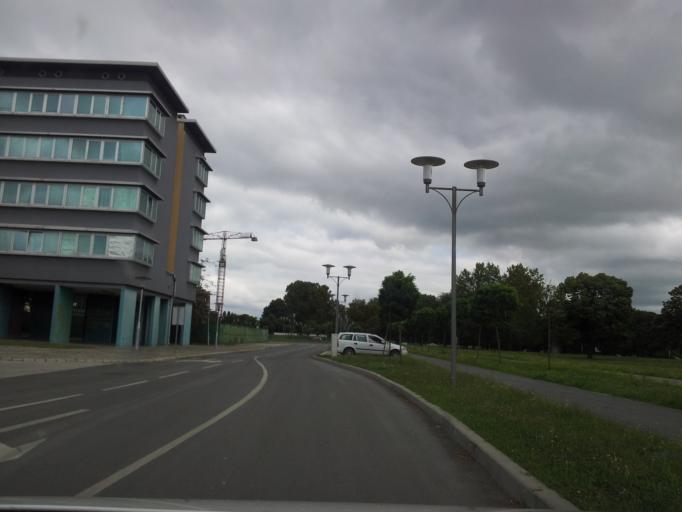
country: HR
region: Osjecko-Baranjska
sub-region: Grad Osijek
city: Osijek
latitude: 45.5557
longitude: 18.7047
